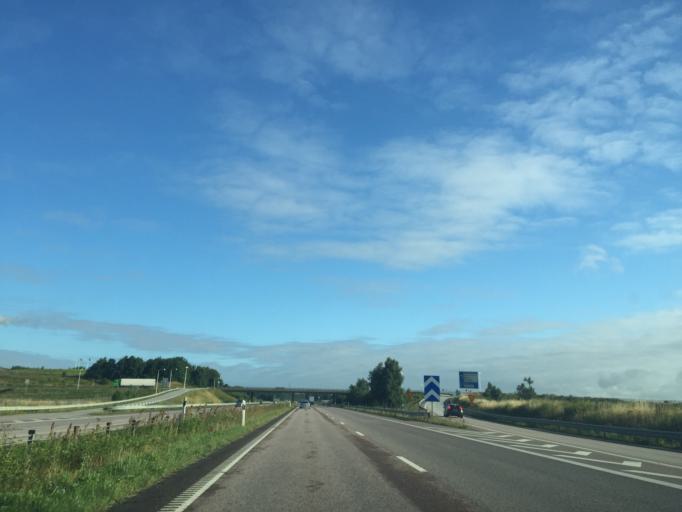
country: SE
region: Skane
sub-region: Helsingborg
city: Odakra
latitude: 56.0621
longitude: 12.7821
